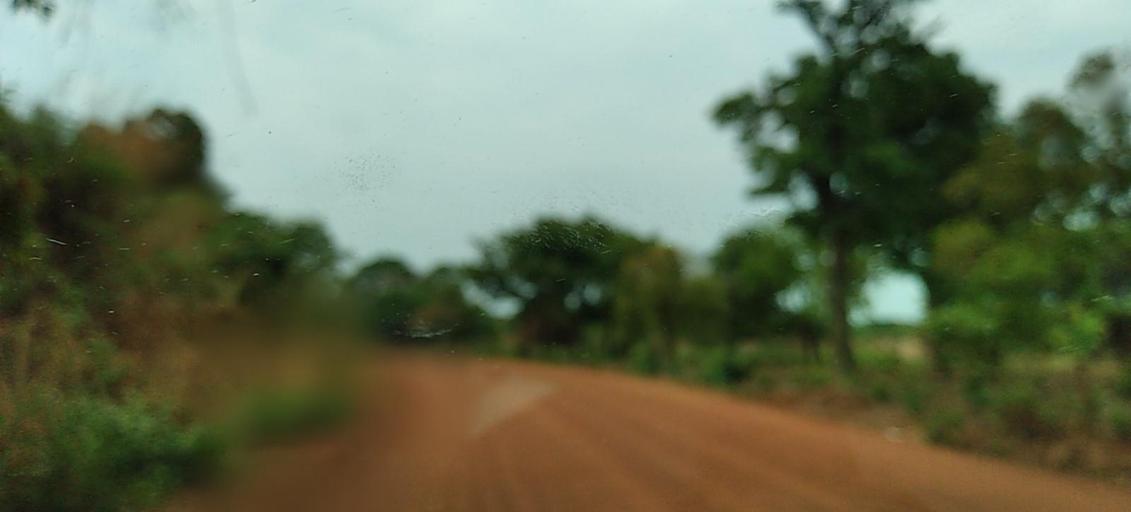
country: ZM
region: North-Western
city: Solwezi
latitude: -12.2339
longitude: 26.5110
